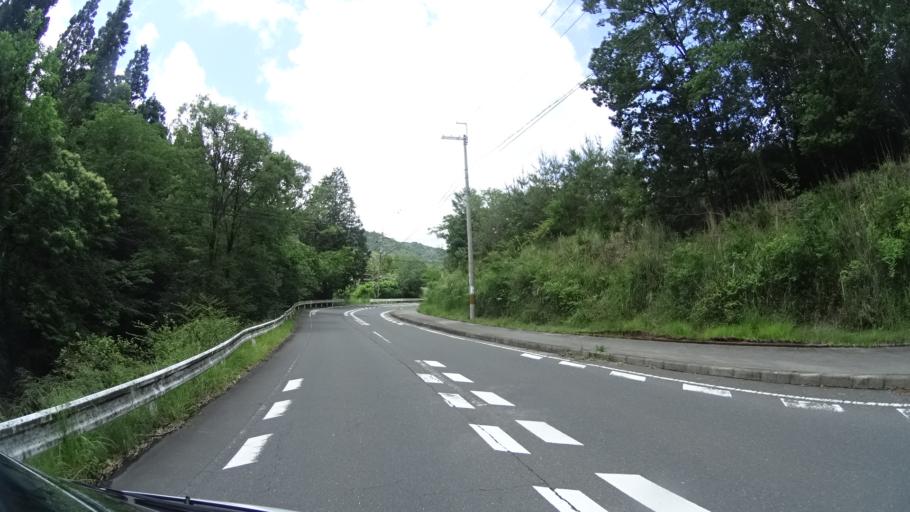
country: JP
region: Kyoto
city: Kameoka
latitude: 35.0174
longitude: 135.4210
